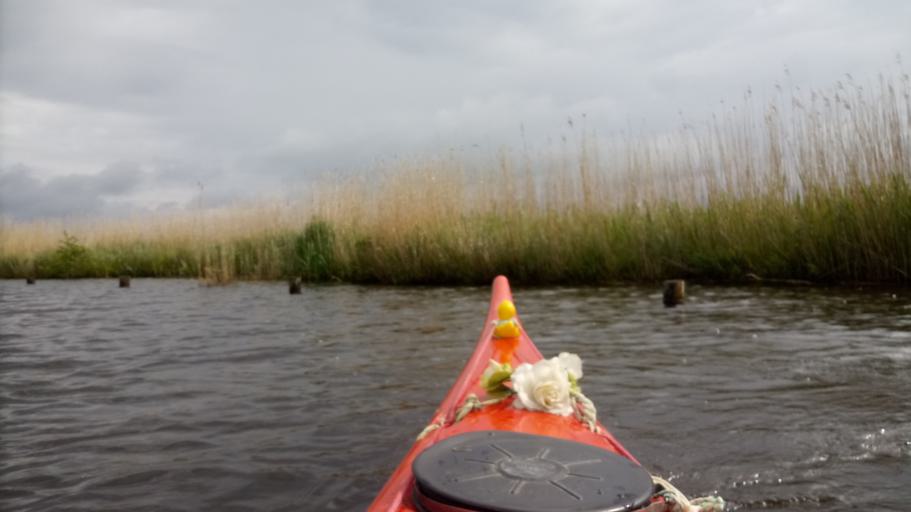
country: NL
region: Overijssel
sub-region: Gemeente Steenwijkerland
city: Sint Jansklooster
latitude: 52.6777
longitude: 6.0496
